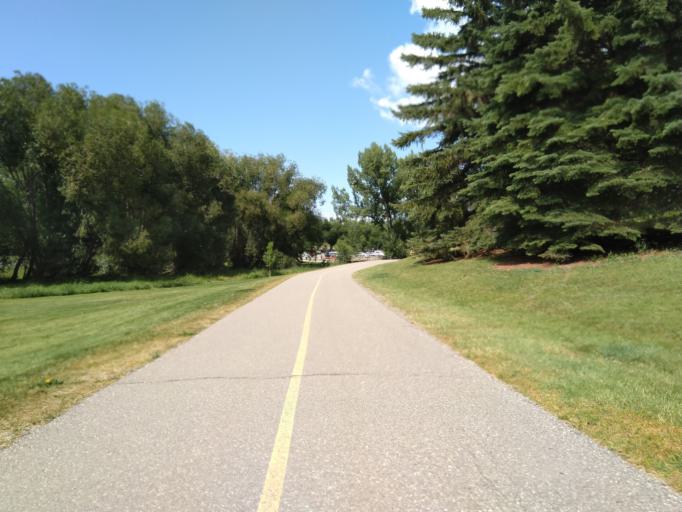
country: CA
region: Alberta
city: Calgary
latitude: 51.0781
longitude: -114.0800
